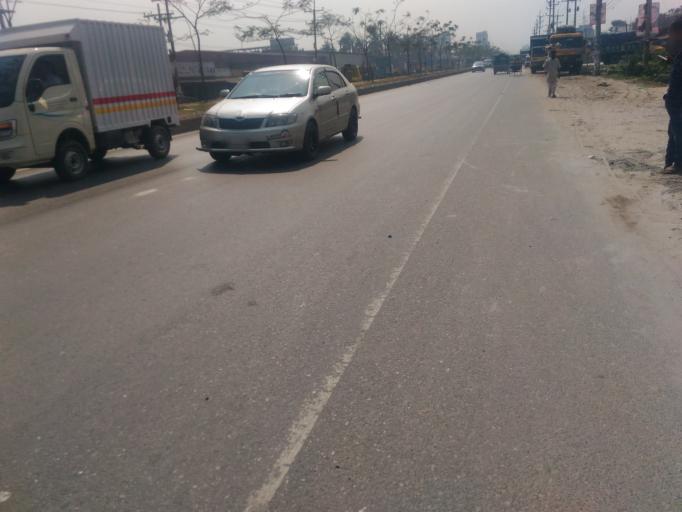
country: BD
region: Dhaka
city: Tungi
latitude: 24.0066
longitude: 90.3833
